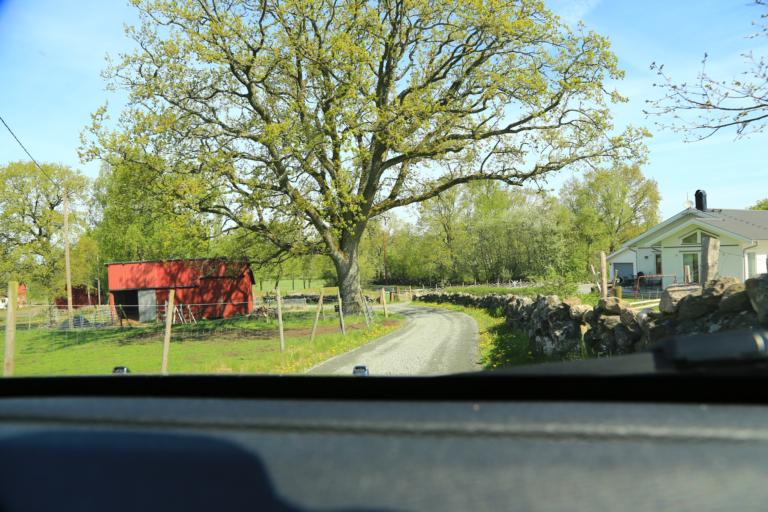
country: SE
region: Halland
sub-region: Varbergs Kommun
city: Varberg
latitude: 57.1541
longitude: 12.2639
